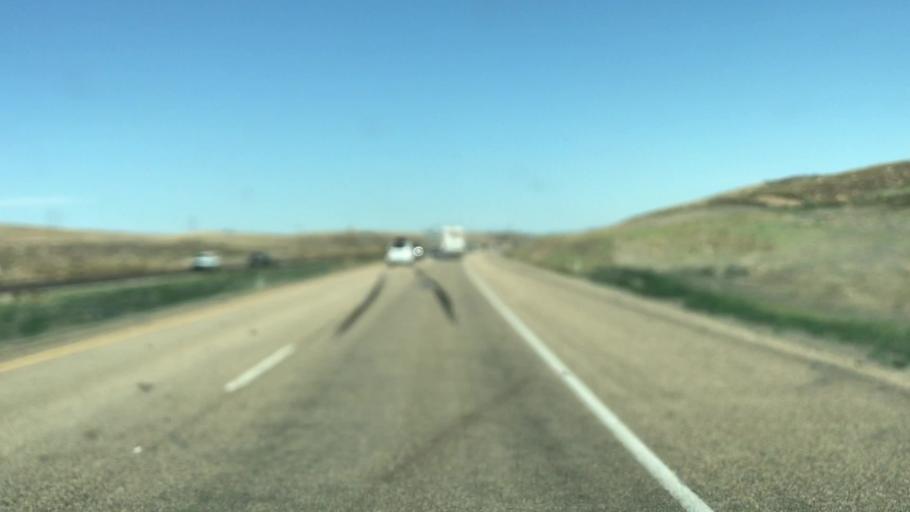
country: US
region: Idaho
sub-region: Payette County
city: New Plymouth
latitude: 43.8828
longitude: -116.8000
